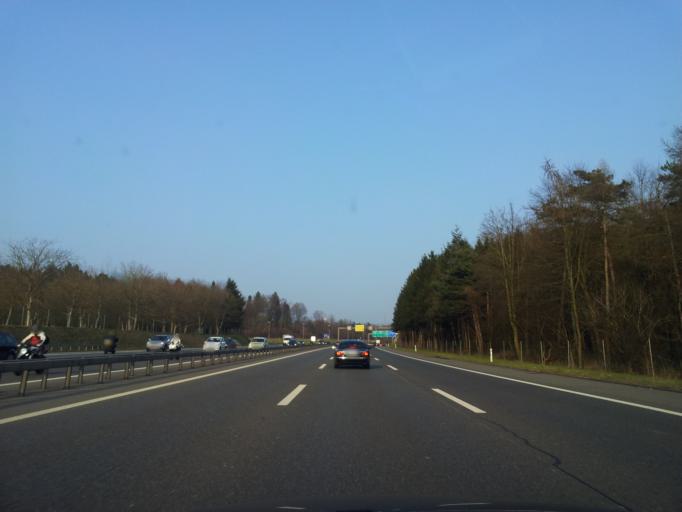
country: CH
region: Aargau
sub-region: Bezirk Baden
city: Birmenstorf
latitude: 47.4546
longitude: 8.2700
